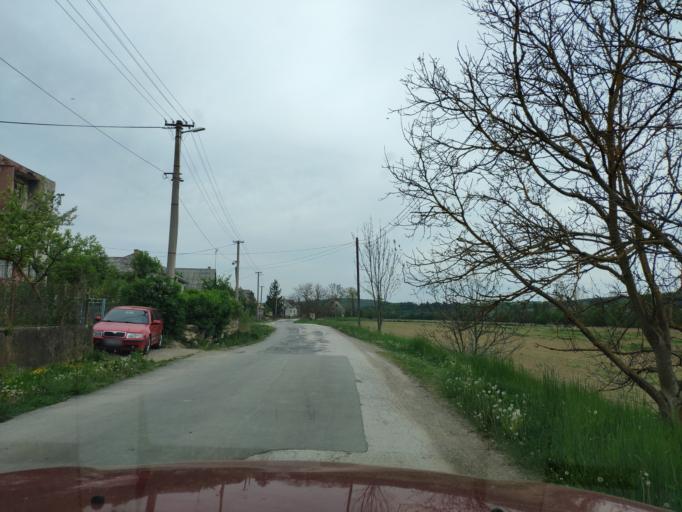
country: SK
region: Banskobystricky
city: Revuca
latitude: 48.5022
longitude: 20.1997
